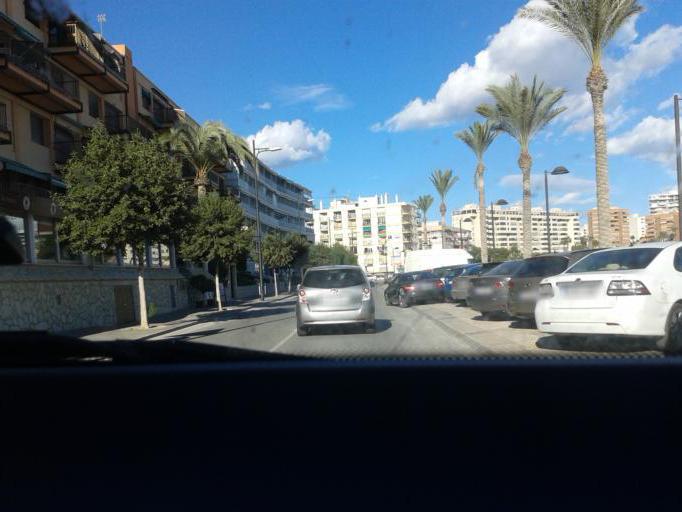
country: ES
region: Valencia
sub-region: Provincia de Alicante
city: el Campello
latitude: 38.4109
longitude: -0.4020
